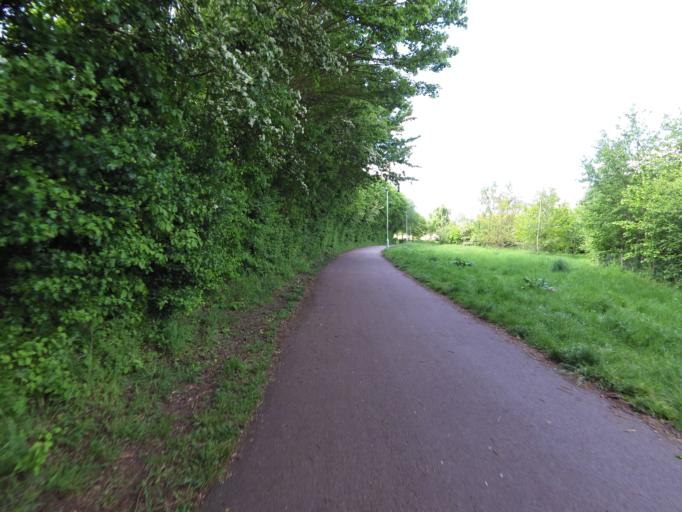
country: GB
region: England
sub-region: Suffolk
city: Great Barton
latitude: 52.2469
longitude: 0.7513
